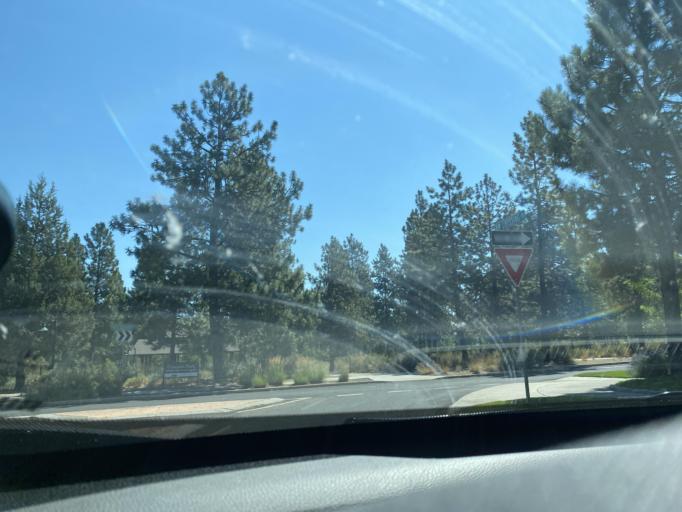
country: US
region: Oregon
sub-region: Deschutes County
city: Bend
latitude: 44.0589
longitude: -121.3525
